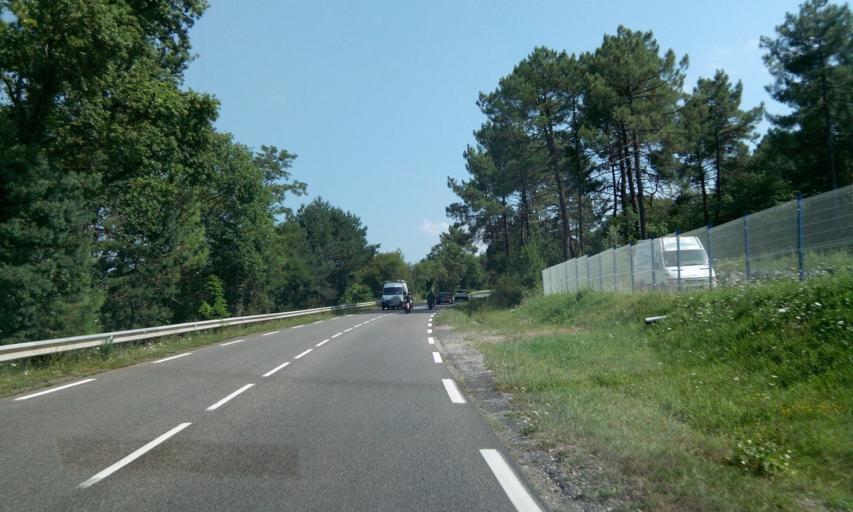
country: FR
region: Limousin
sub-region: Departement de la Correze
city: Cosnac
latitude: 45.1081
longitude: 1.5700
